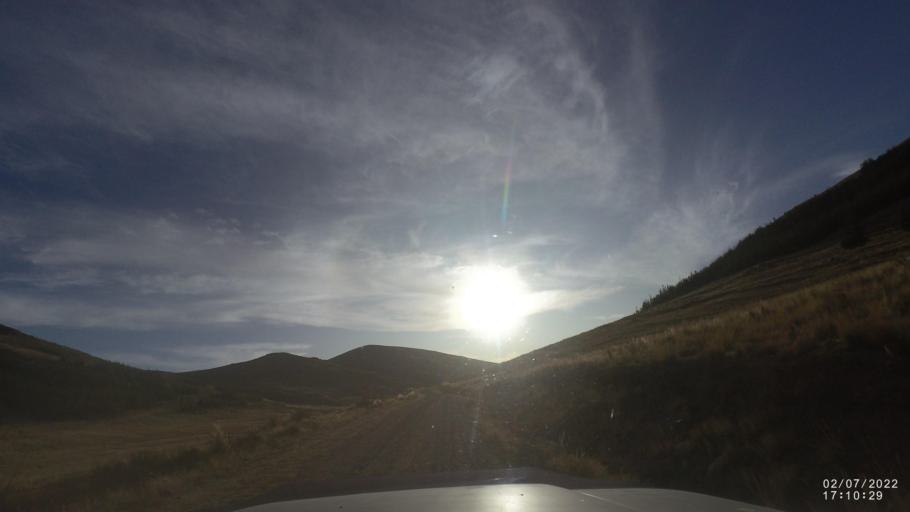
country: BO
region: Cochabamba
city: Irpa Irpa
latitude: -17.8965
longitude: -66.5580
